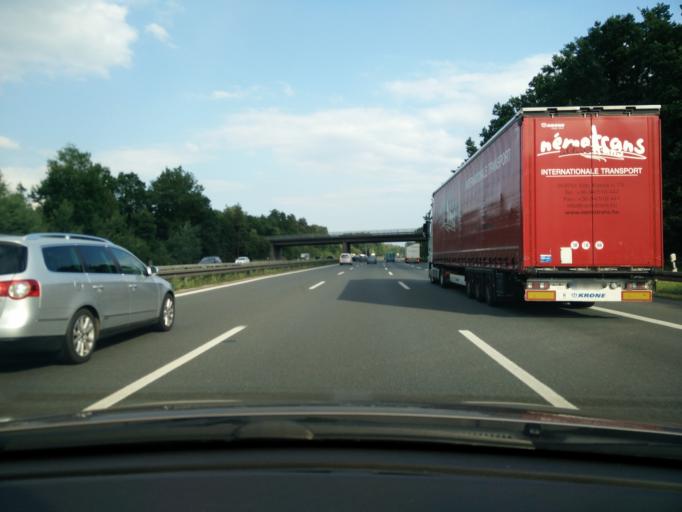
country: DE
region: Bavaria
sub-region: Regierungsbezirk Mittelfranken
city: Wetzendorf
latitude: 49.5291
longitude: 11.0611
